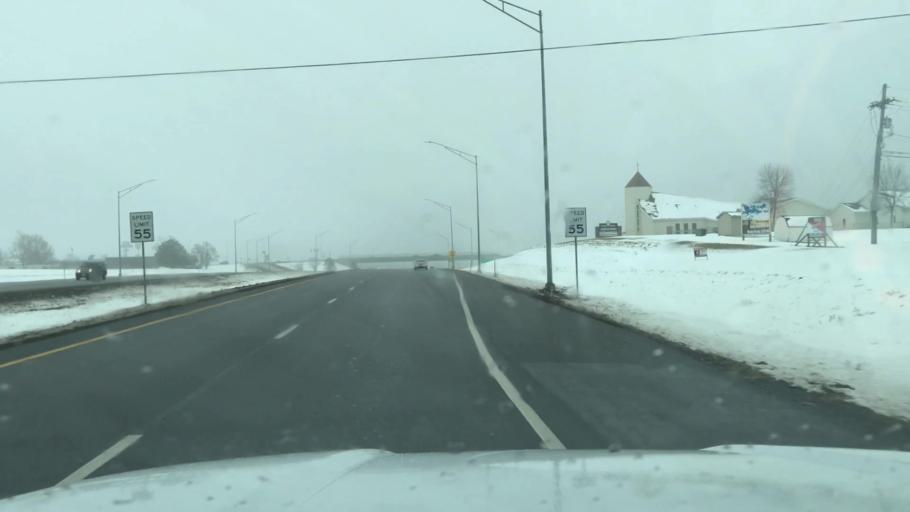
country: US
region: Missouri
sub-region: Clinton County
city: Cameron
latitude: 39.7544
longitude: -94.2397
